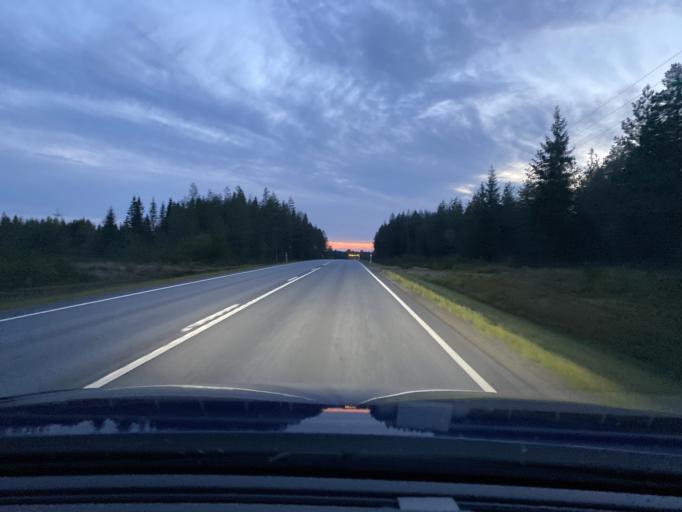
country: FI
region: Southern Ostrobothnia
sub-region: Suupohja
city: Kauhajoki
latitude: 62.4591
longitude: 22.1376
